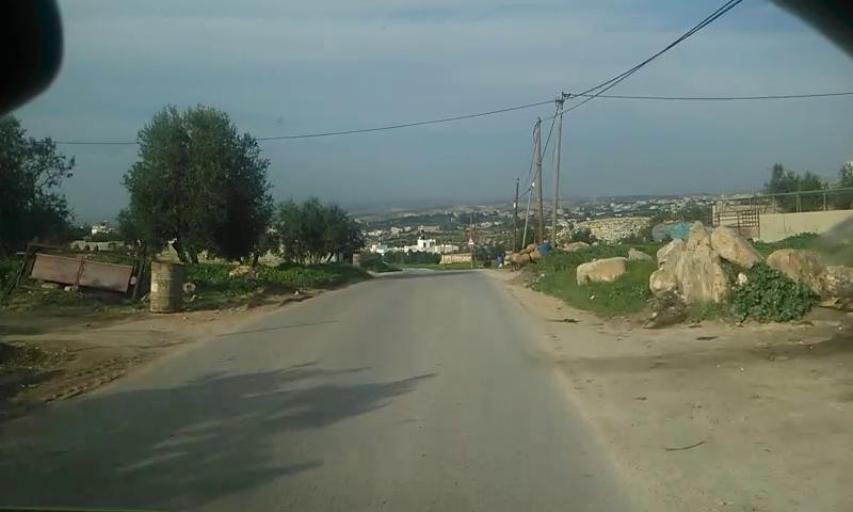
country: PS
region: West Bank
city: Bayt Ula
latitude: 31.6082
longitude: 35.0157
